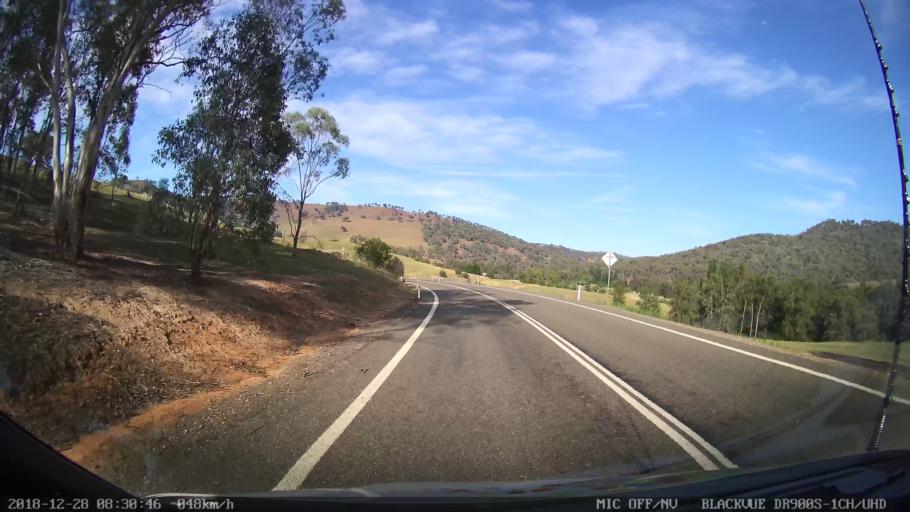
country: AU
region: New South Wales
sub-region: Blayney
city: Blayney
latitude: -33.9570
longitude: 149.3227
